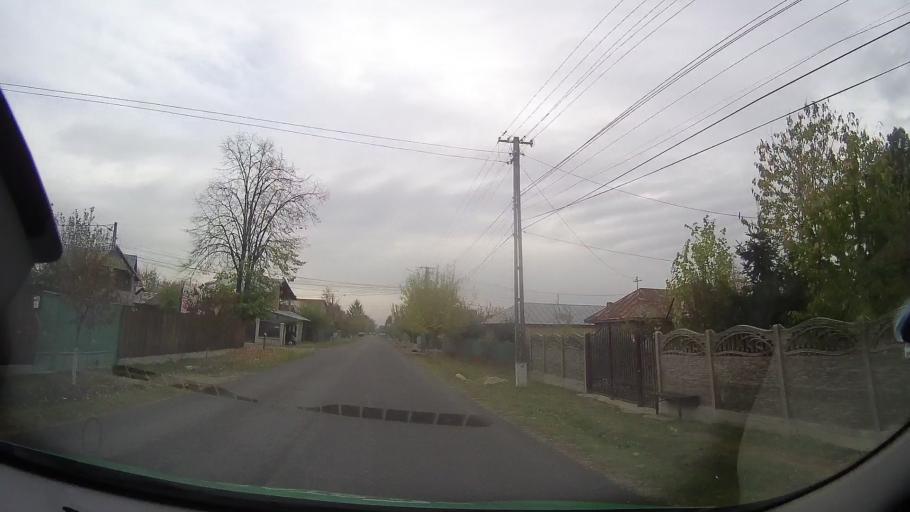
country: RO
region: Prahova
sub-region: Comuna Valea Calugareasca
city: Pantazi
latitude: 44.9379
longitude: 26.1367
